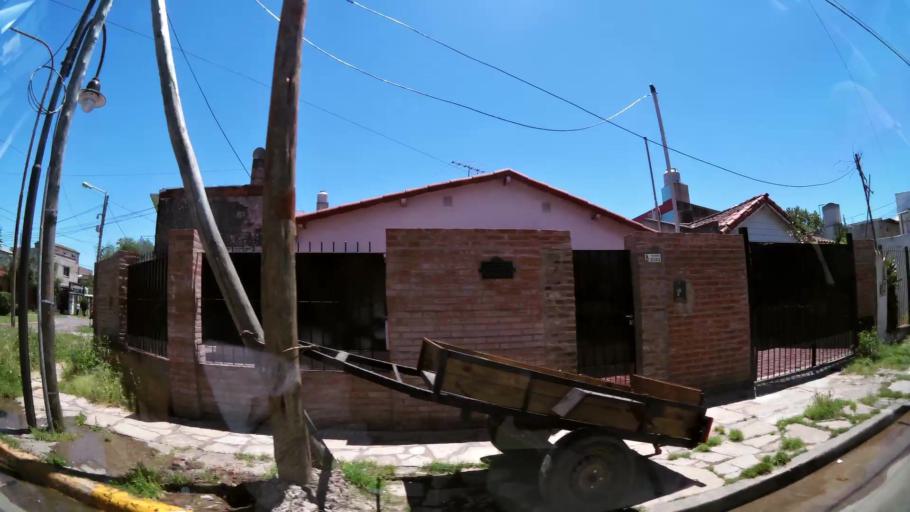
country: AR
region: Buenos Aires
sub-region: Partido de Tigre
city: Tigre
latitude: -34.4519
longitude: -58.5585
